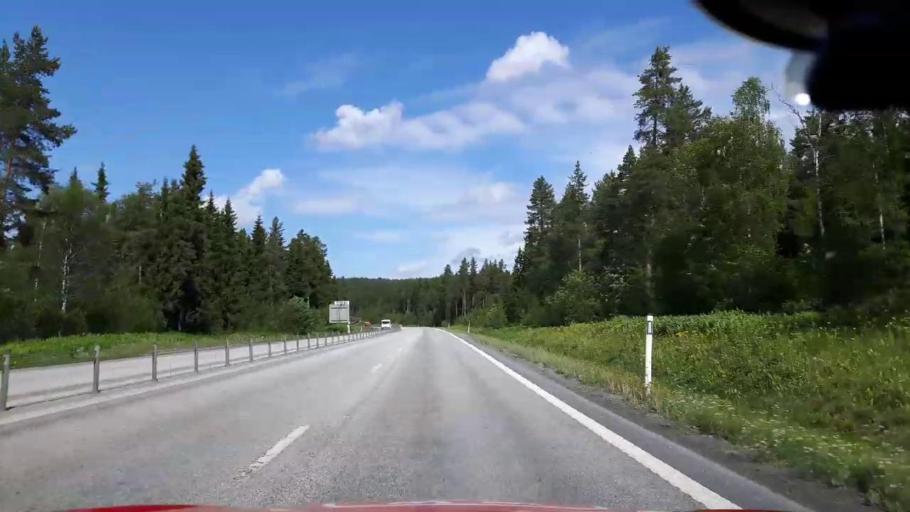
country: SE
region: Jaemtland
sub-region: OEstersunds Kommun
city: Ostersund
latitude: 63.1873
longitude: 14.6895
